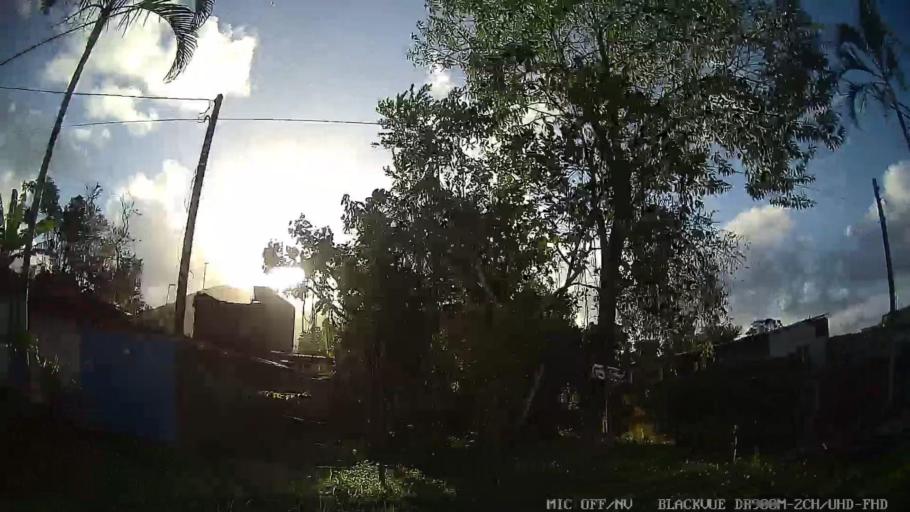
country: BR
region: Sao Paulo
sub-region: Itanhaem
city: Itanhaem
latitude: -24.1379
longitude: -46.7235
